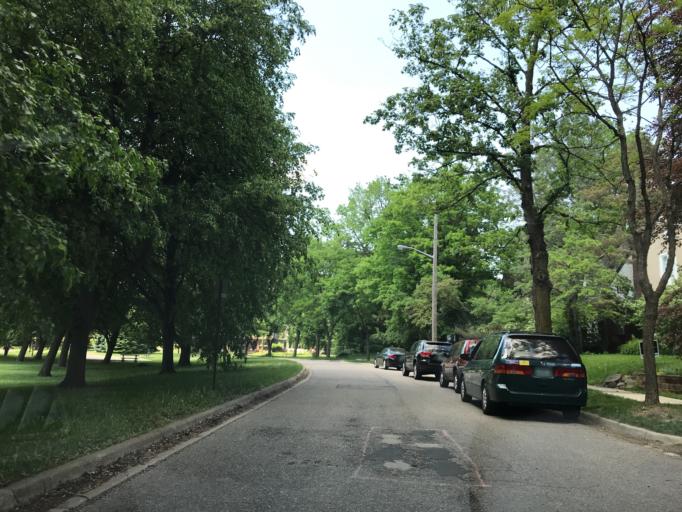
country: US
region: Michigan
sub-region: Washtenaw County
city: Ann Arbor
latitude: 42.2657
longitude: -83.7264
